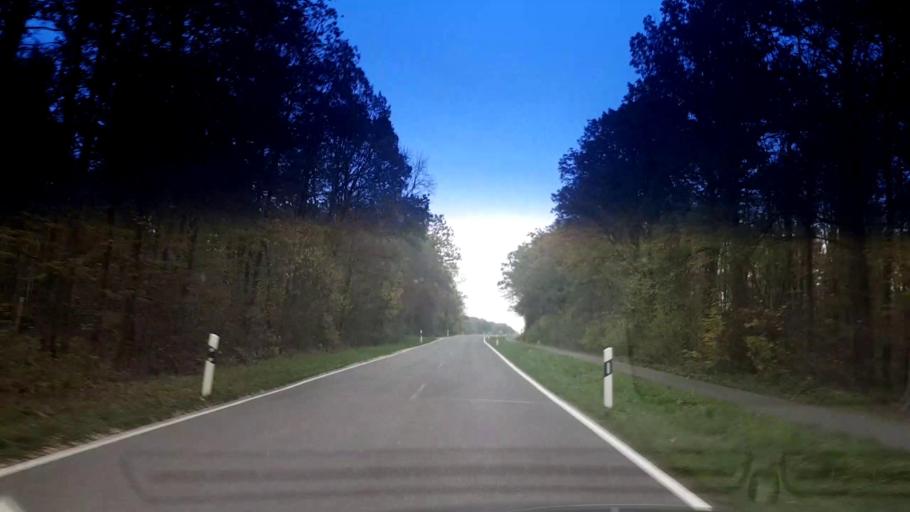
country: DE
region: Bavaria
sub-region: Upper Franconia
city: Memmelsdorf
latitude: 49.9329
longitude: 10.9698
